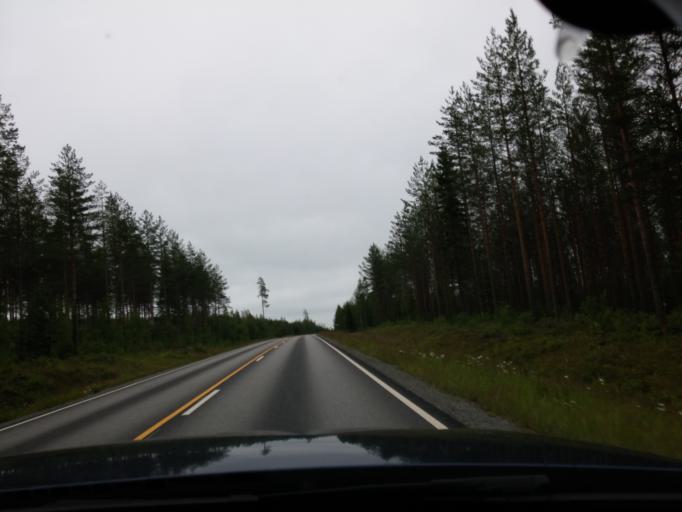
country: FI
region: Central Finland
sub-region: Saarijaervi-Viitasaari
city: Saarijaervi
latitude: 62.6794
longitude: 25.1818
